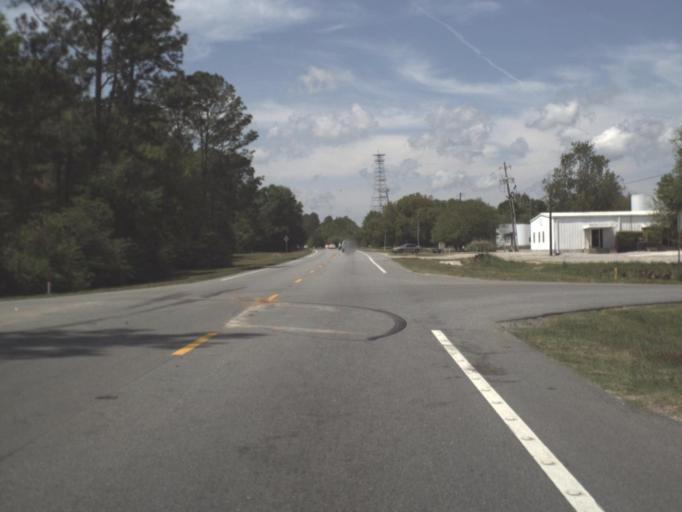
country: US
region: Florida
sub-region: Escambia County
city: Cantonment
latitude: 30.5360
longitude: -87.3974
